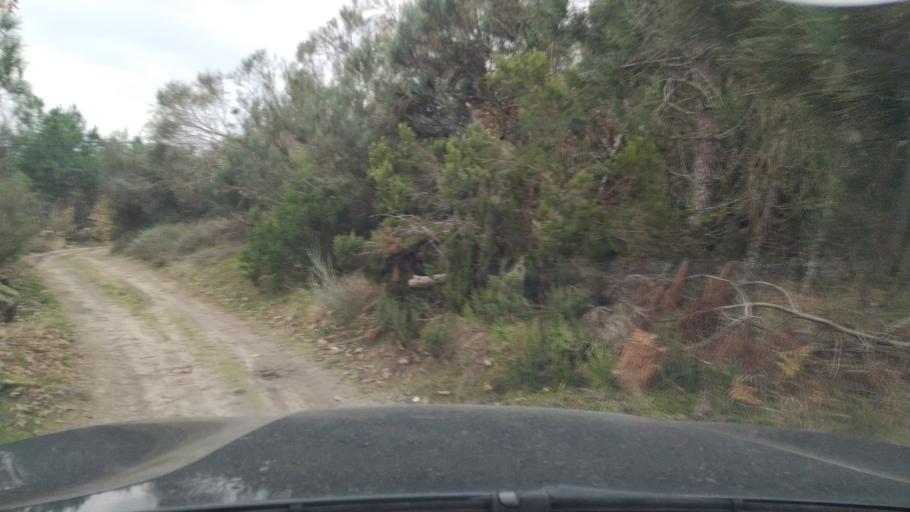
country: PT
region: Vila Real
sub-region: Sabrosa
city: Sabrosa
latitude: 41.3379
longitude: -7.6299
